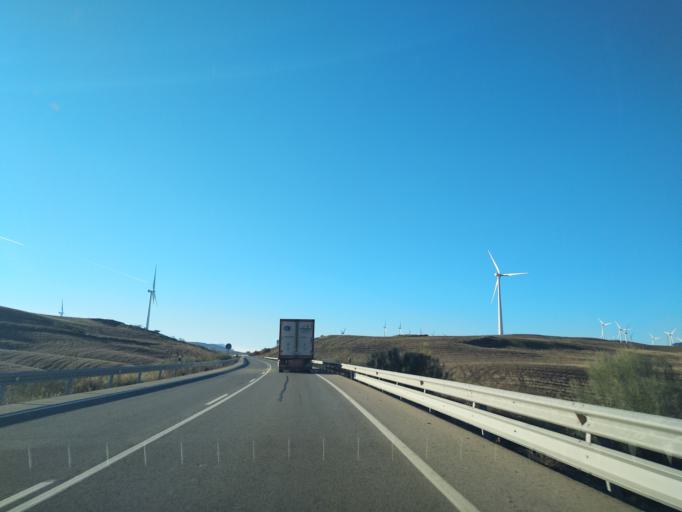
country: ES
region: Andalusia
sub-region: Provincia de Malaga
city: Teba
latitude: 36.9477
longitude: -4.8659
